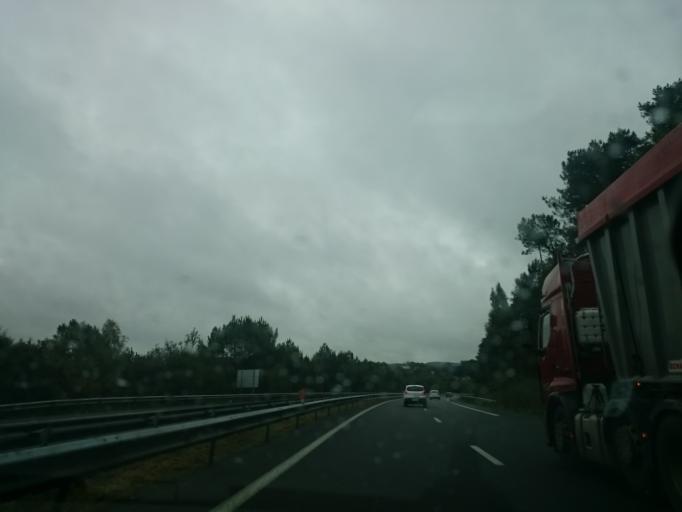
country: FR
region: Brittany
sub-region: Departement du Morbihan
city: Nivillac
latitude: 47.5320
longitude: -2.2963
